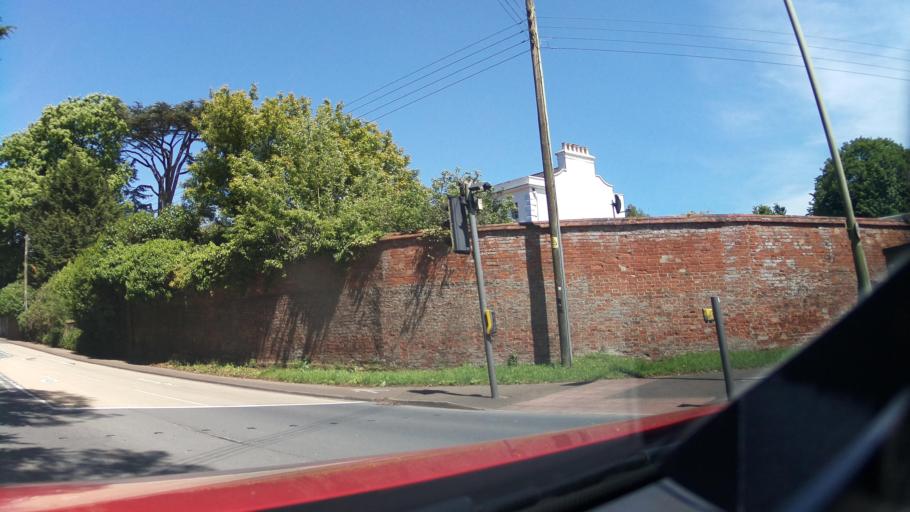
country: GB
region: England
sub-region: Devon
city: Topsham
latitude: 50.6823
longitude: -3.4442
